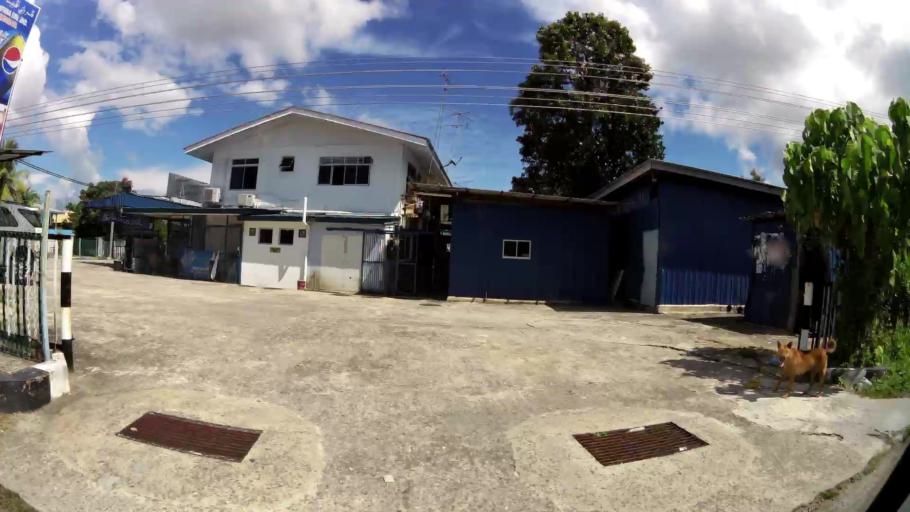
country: BN
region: Brunei and Muara
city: Bandar Seri Begawan
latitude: 4.9698
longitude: 114.9406
